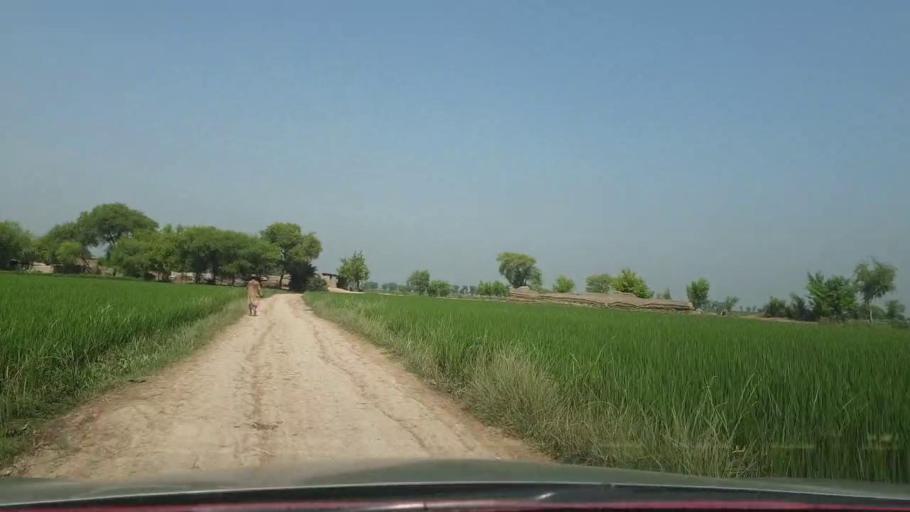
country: PK
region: Sindh
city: Kambar
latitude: 27.5938
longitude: 67.9076
